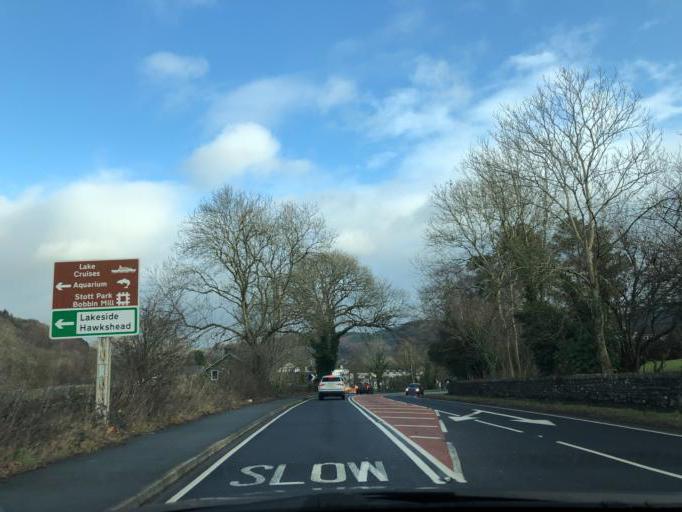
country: GB
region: England
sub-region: Cumbria
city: Grange-over-Sands
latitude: 54.2683
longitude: -2.9730
